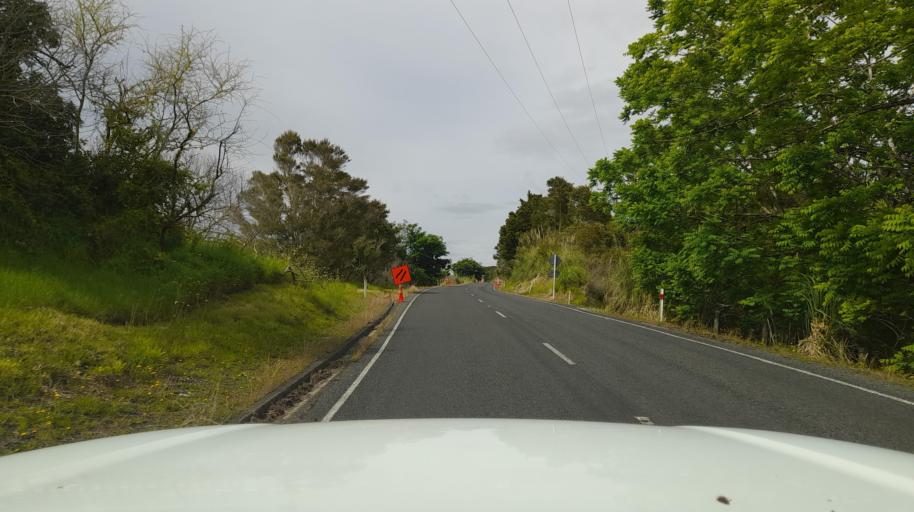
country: NZ
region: Northland
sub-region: Far North District
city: Taipa
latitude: -35.2619
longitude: 173.5255
